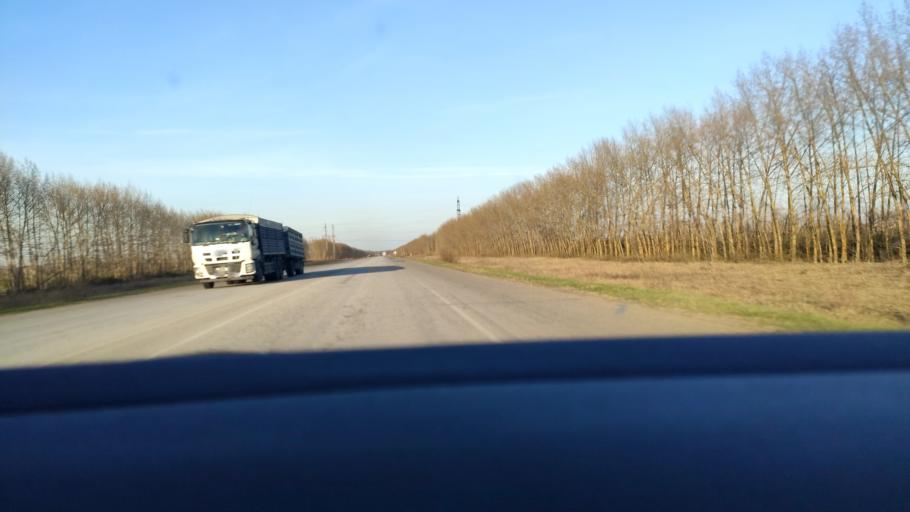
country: RU
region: Voronezj
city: Kolodeznyy
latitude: 51.4156
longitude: 39.2703
